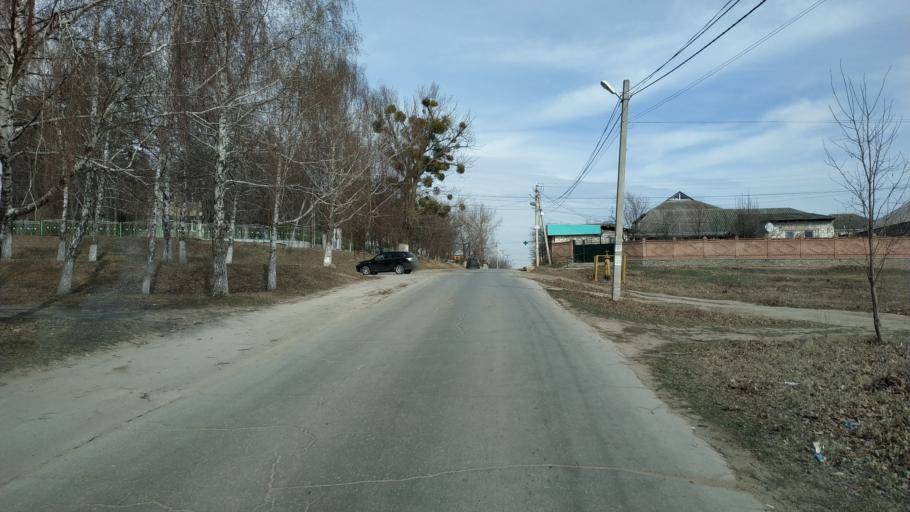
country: MD
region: Chisinau
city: Vatra
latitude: 47.0950
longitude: 28.6769
